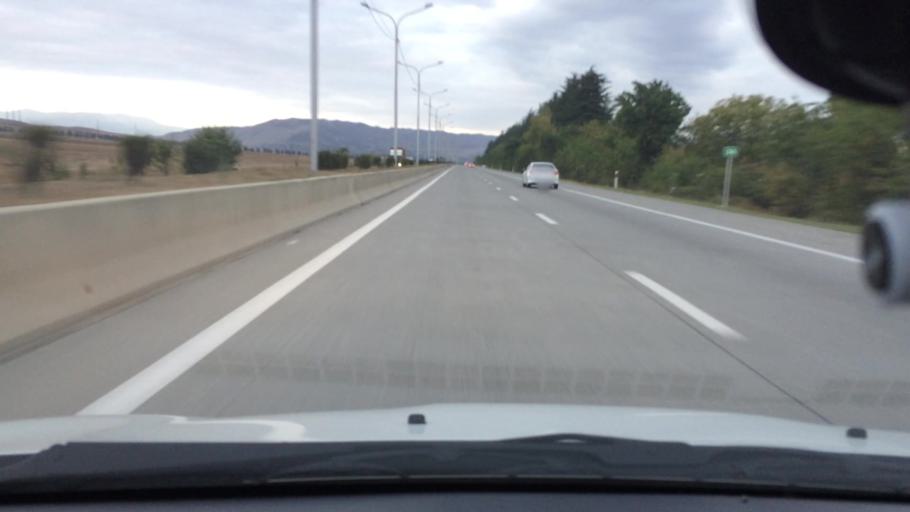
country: GE
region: Mtskheta-Mtianeti
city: Mtskheta
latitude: 41.8968
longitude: 44.6183
